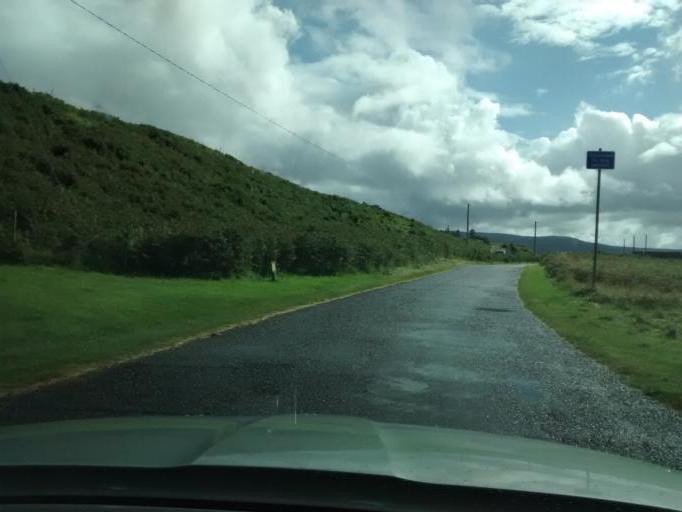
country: GB
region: Scotland
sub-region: North Ayrshire
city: Isle of Arran
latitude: 55.5606
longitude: -5.3453
